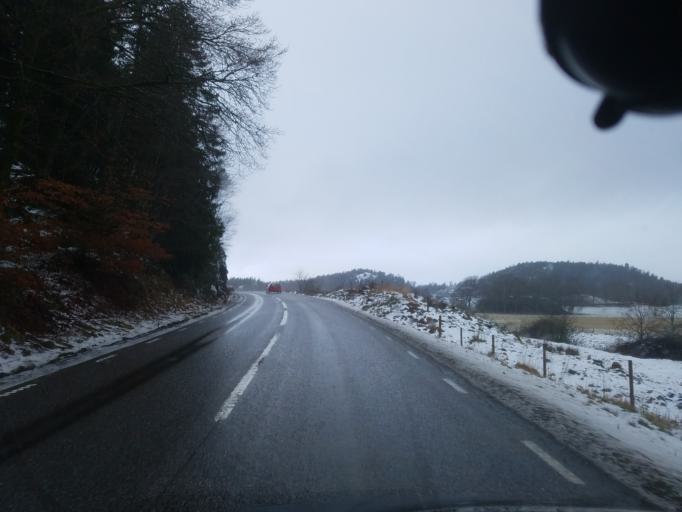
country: SE
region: Vaestra Goetaland
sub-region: Orust
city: Henan
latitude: 58.3443
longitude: 11.6708
